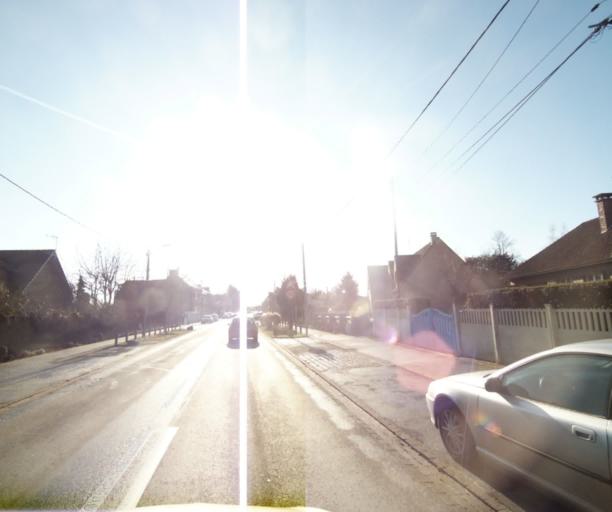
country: FR
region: Nord-Pas-de-Calais
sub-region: Departement du Nord
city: Aulnoy-lez-Valenciennes
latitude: 50.3326
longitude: 3.5235
